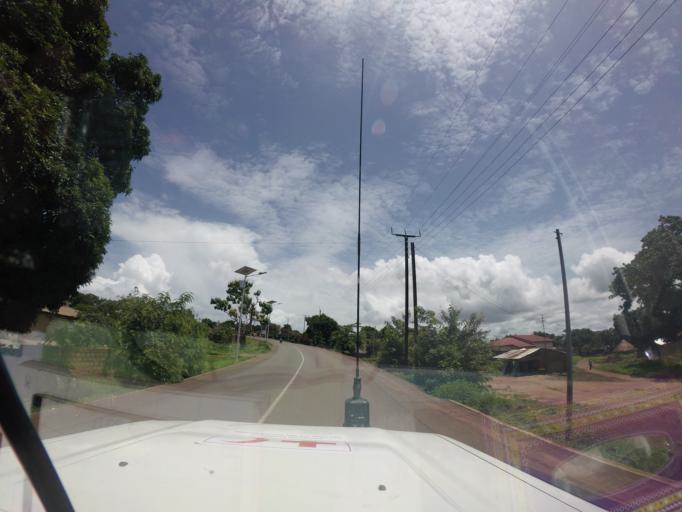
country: GN
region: Faranah
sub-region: Faranah Prefecture
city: Faranah
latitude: 10.0422
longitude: -10.7549
